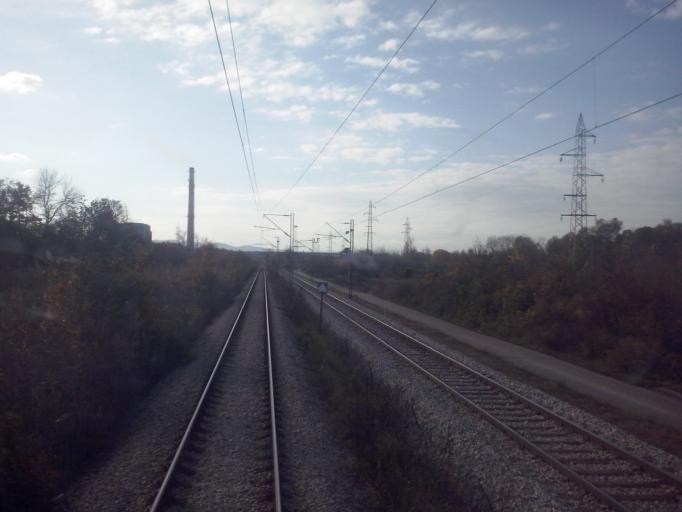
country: RS
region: Central Serbia
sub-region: Belgrade
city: Lazarevac
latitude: 44.4368
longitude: 20.2787
